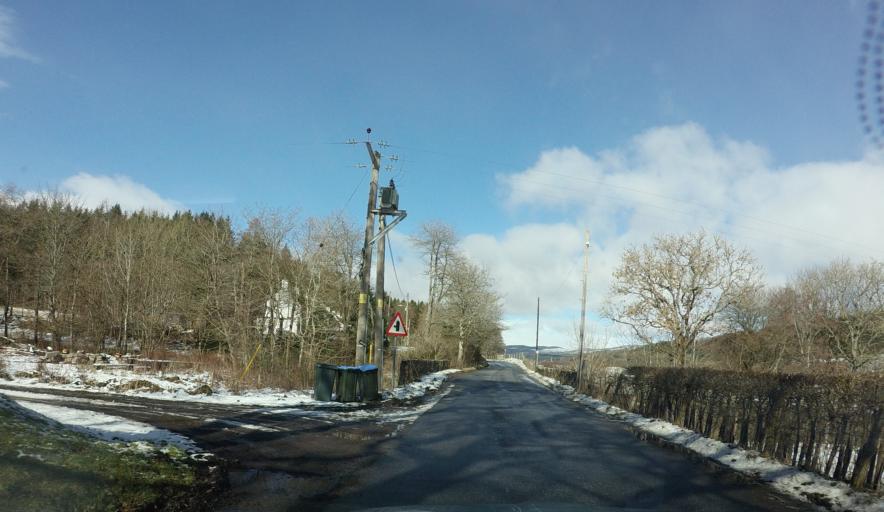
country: GB
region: Scotland
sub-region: Perth and Kinross
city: Bankfoot
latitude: 56.5822
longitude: -3.6277
